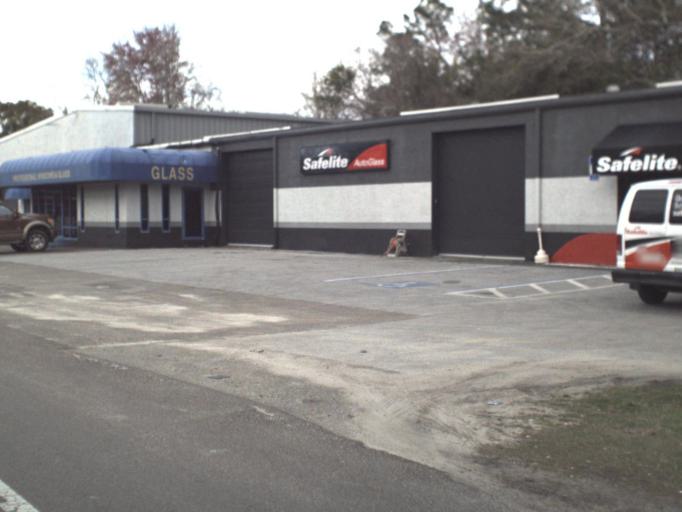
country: US
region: Florida
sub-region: Bay County
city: Hiland Park
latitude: 30.1989
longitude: -85.6249
